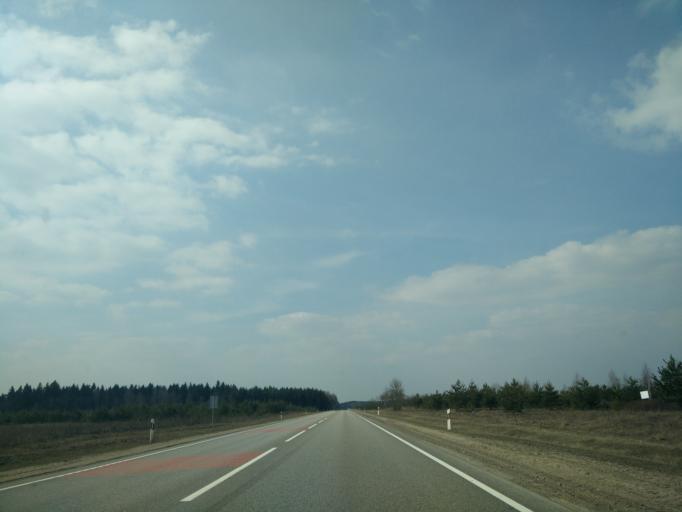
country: LT
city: Lentvaris
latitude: 54.6211
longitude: 25.0532
